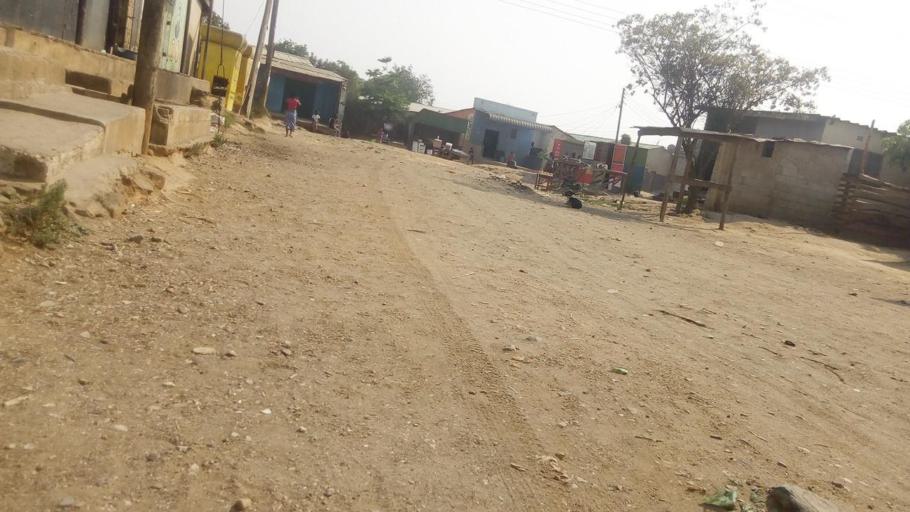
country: ZM
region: Lusaka
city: Lusaka
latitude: -15.3571
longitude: 28.2899
